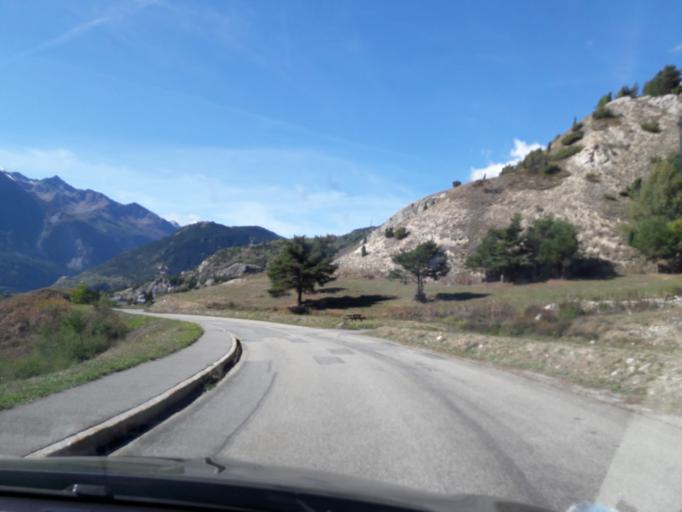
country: FR
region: Rhone-Alpes
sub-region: Departement de la Savoie
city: Modane
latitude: 45.2147
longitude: 6.7047
